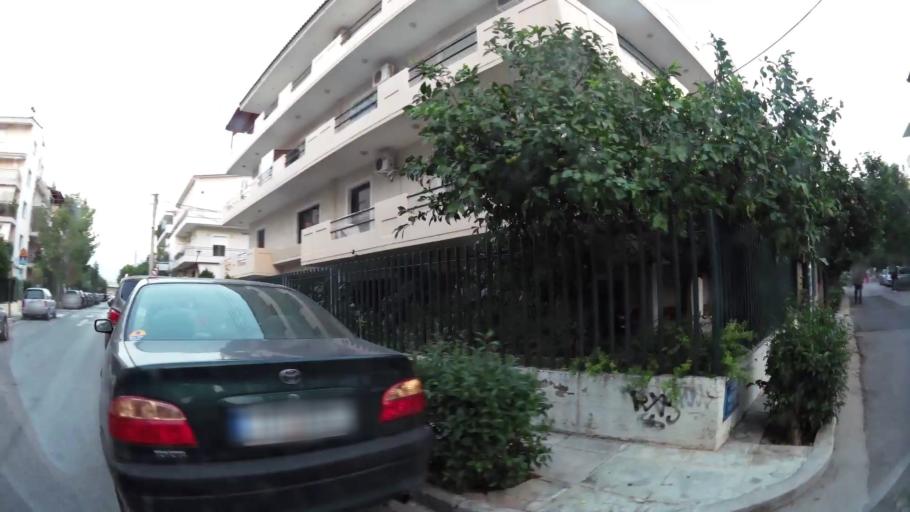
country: GR
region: Attica
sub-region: Nomarchia Athinas
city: Agia Paraskevi
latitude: 38.0209
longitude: 23.8336
